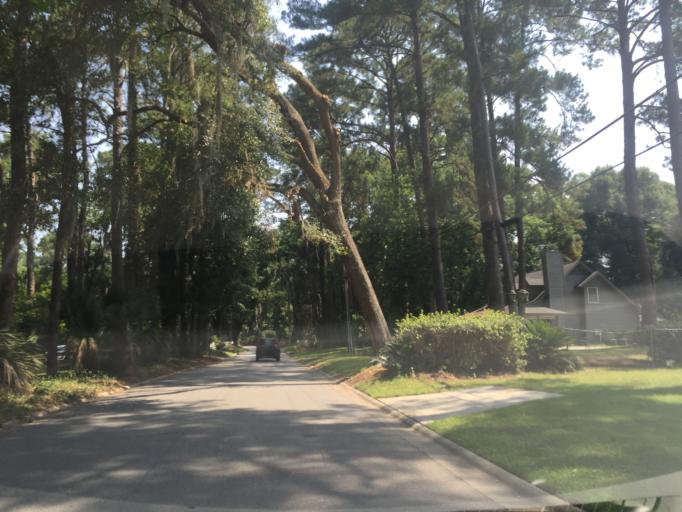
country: US
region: Georgia
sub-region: Chatham County
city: Montgomery
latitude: 31.9695
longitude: -81.1294
